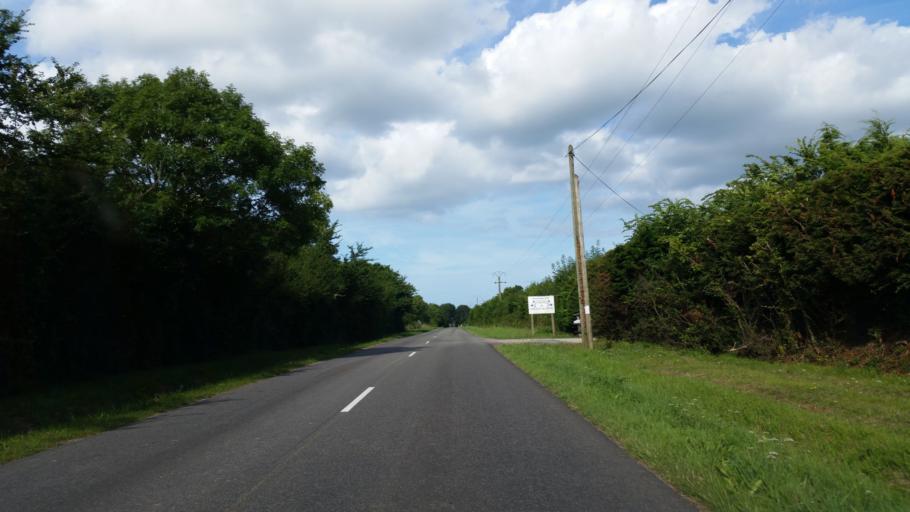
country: FR
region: Lower Normandy
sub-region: Departement de la Manche
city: Sainte-Mere-Eglise
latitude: 49.4504
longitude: -1.2756
